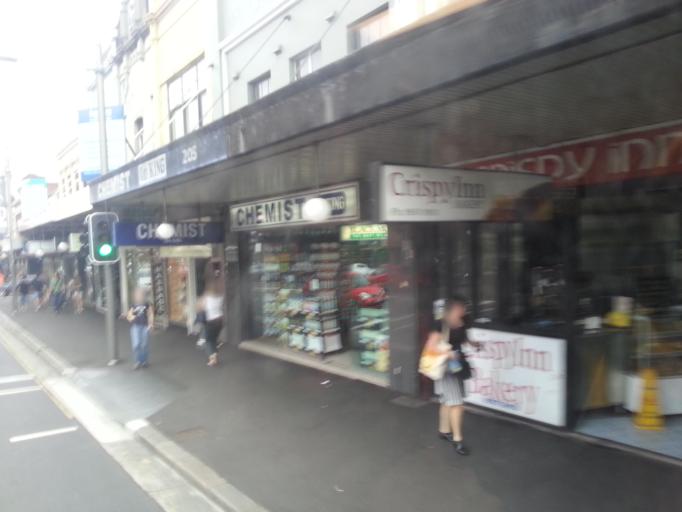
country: AU
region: New South Wales
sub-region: Marrickville
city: Newtown
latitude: -33.8949
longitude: 151.1819
